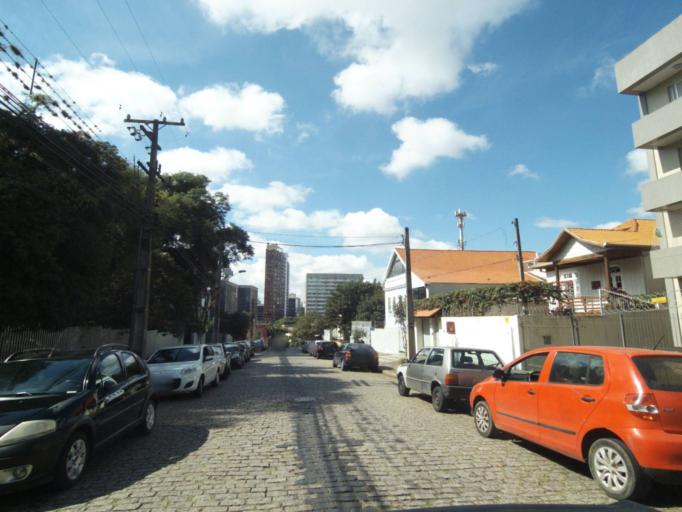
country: BR
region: Parana
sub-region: Curitiba
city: Curitiba
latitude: -25.4195
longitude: -49.2724
